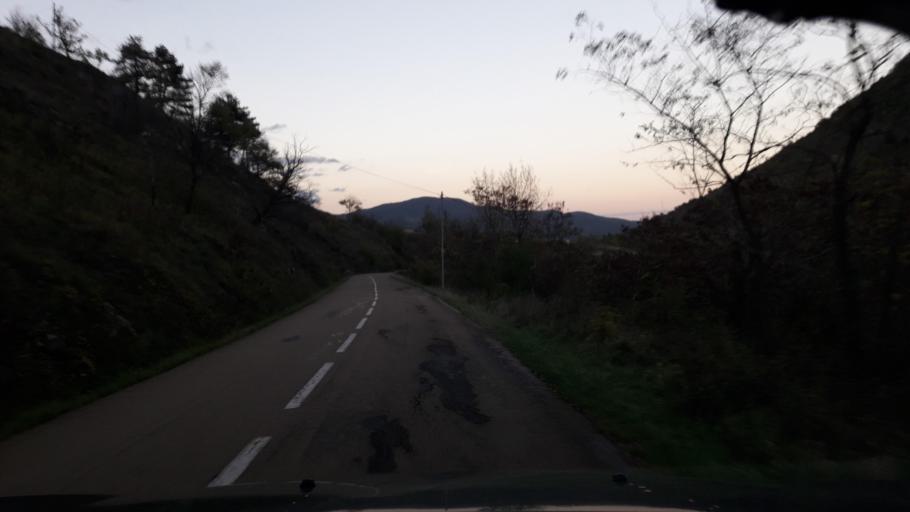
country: FR
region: Rhone-Alpes
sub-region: Departement de l'Ardeche
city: Saint-Priest
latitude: 44.7060
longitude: 4.5735
